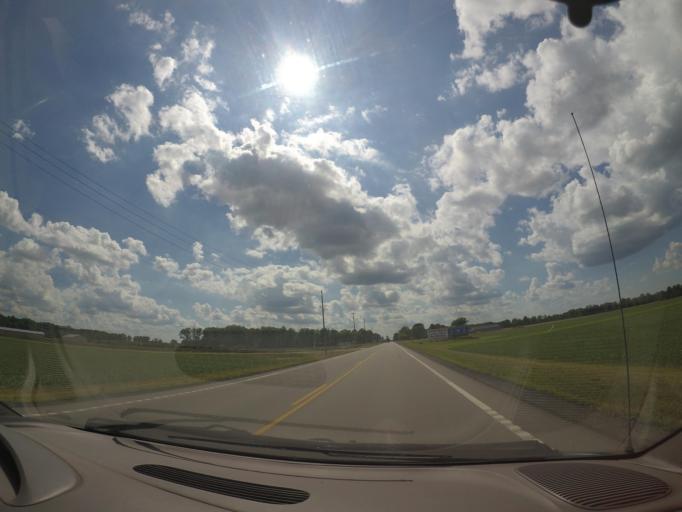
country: US
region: Ohio
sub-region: Huron County
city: Norwalk
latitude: 41.2494
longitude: -82.5548
